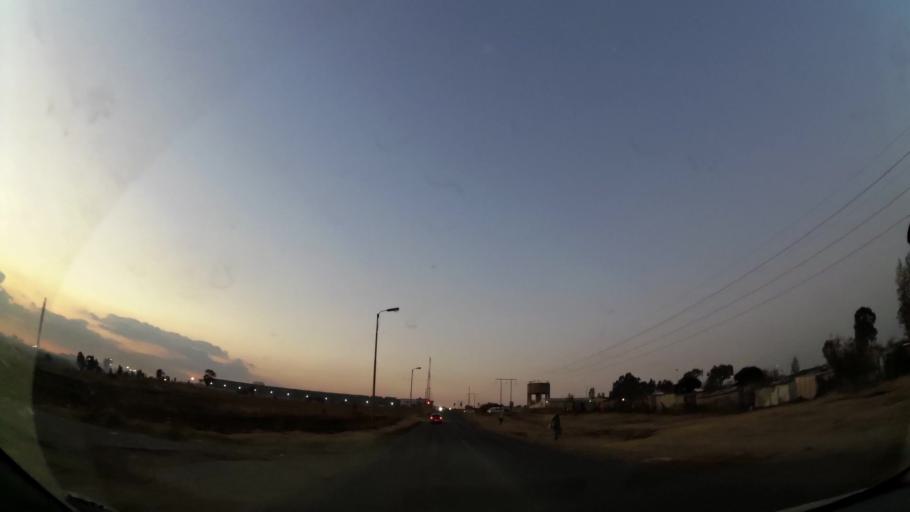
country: ZA
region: Gauteng
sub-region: Ekurhuleni Metropolitan Municipality
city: Springs
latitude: -26.2932
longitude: 28.3832
